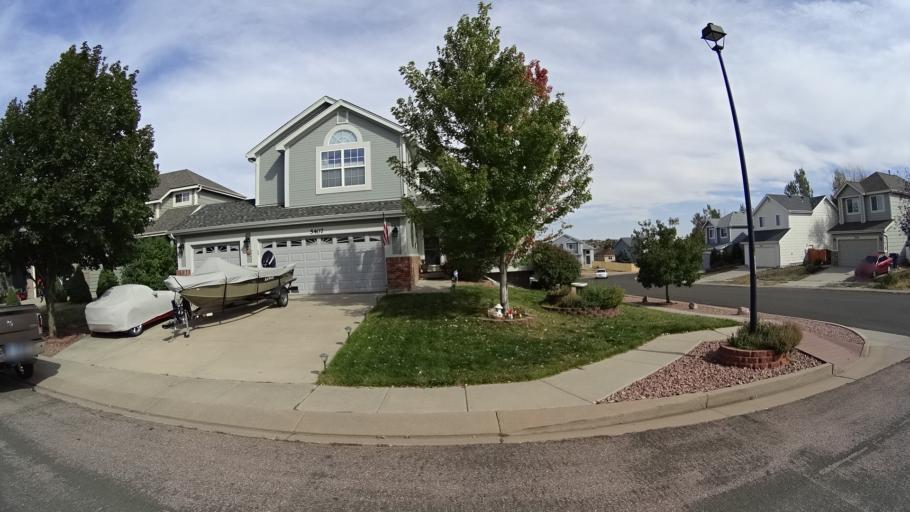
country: US
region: Colorado
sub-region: El Paso County
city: Cimarron Hills
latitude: 38.9112
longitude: -104.6941
